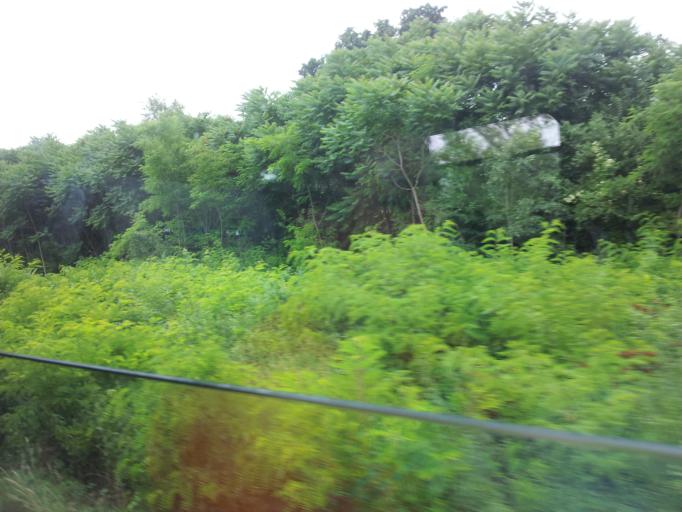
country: HU
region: Veszprem
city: Revfueloep
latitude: 46.8335
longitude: 17.6465
